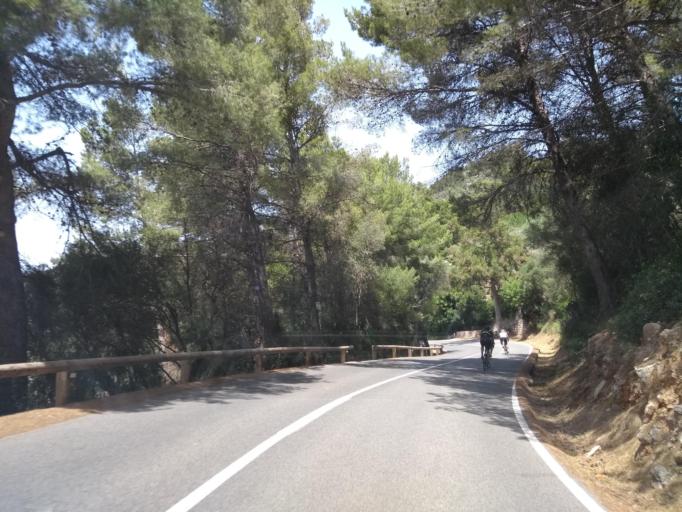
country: ES
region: Balearic Islands
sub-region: Illes Balears
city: Soller
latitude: 39.7796
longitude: 2.7180
